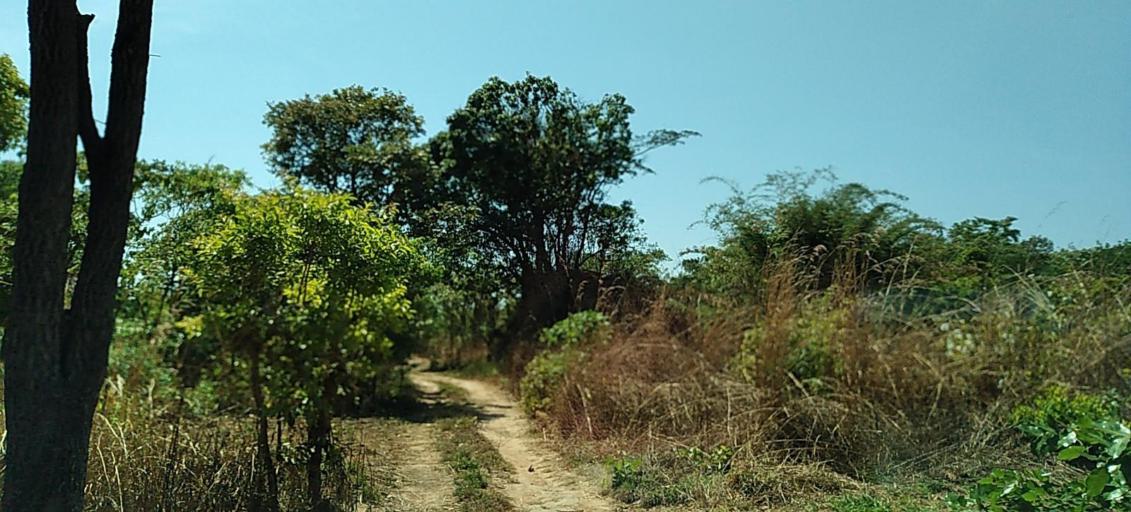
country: ZM
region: Copperbelt
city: Chililabombwe
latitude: -12.2885
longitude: 27.8886
